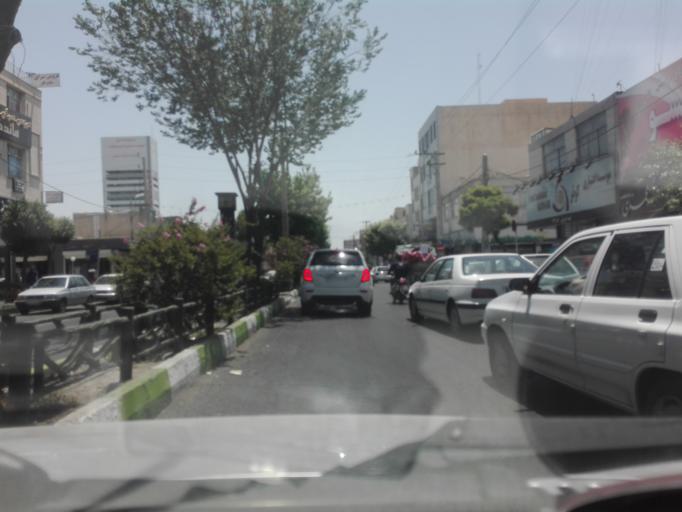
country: IR
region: Tehran
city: Shahre Jadide Andisheh
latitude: 35.7215
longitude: 50.9876
